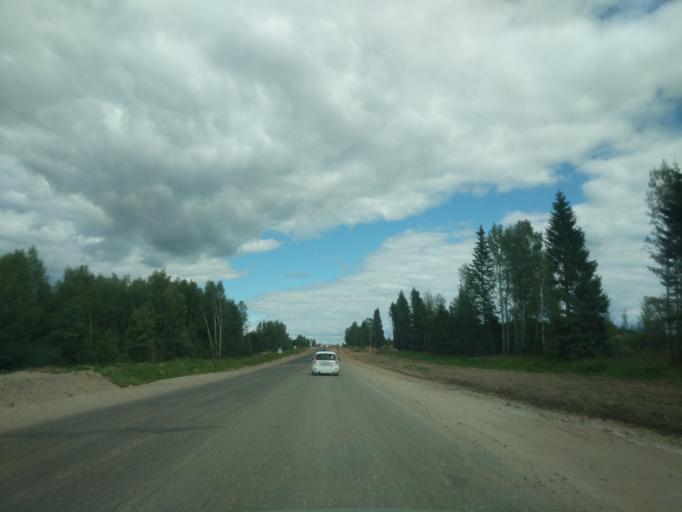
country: RU
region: Kostroma
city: Sudislavl'
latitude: 57.8680
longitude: 41.6375
